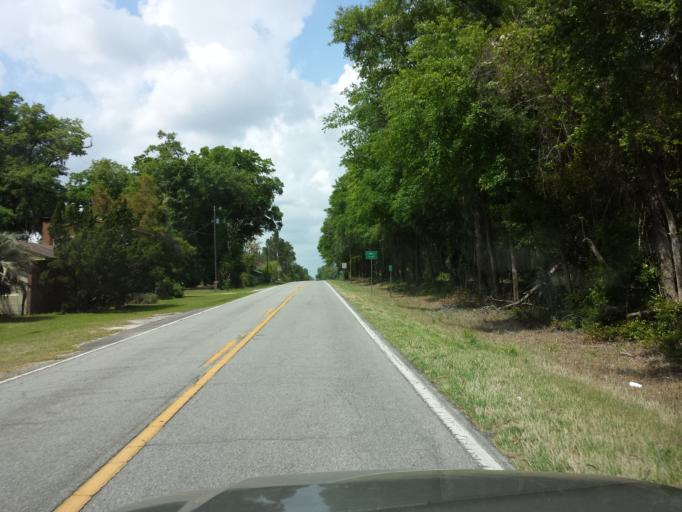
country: US
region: Georgia
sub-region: Echols County
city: Statenville
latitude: 30.6409
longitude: -83.1353
